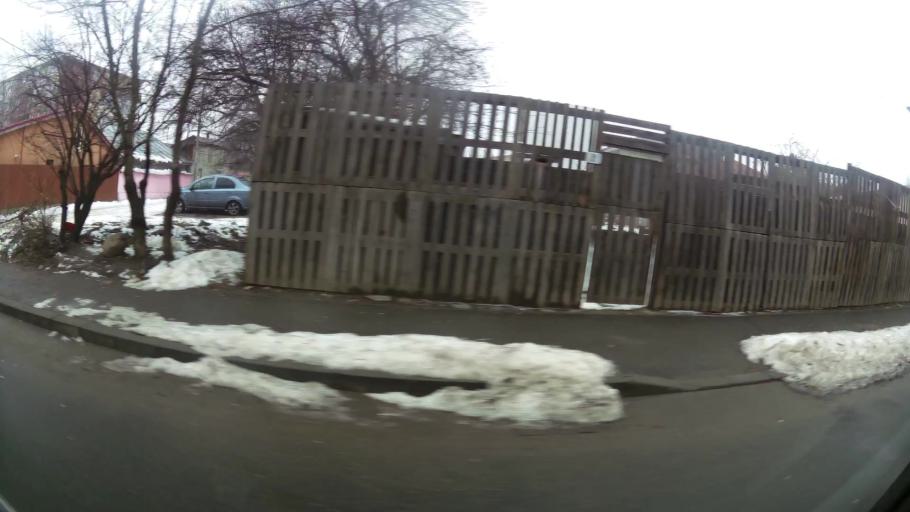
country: RO
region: Ilfov
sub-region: Comuna Chiajna
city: Rosu
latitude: 44.4412
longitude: 26.0128
